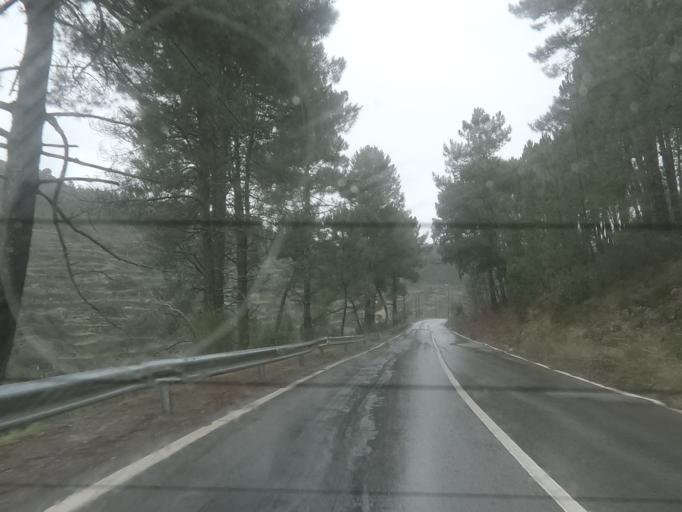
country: PT
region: Vila Real
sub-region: Vila Real
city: Vila Real
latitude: 41.2506
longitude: -7.6884
